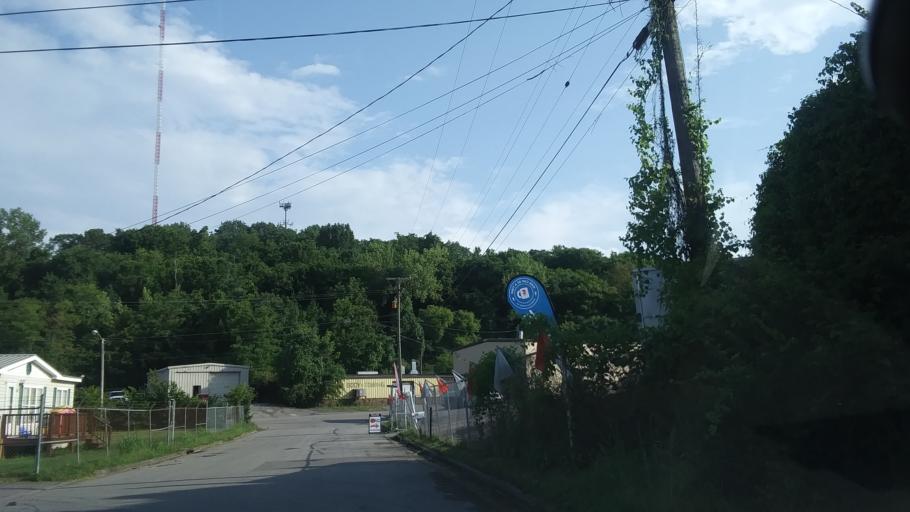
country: US
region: Tennessee
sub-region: Davidson County
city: Belle Meade
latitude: 36.1470
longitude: -86.8672
